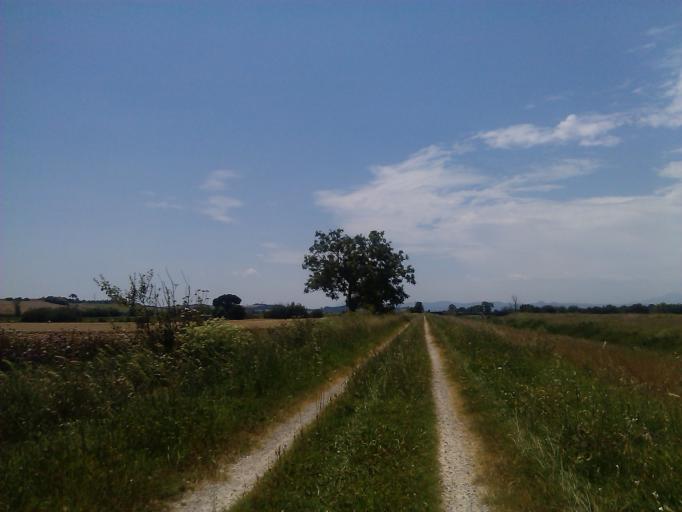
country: IT
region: Tuscany
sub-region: Province of Arezzo
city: Foiano della Chiana
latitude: 43.2853
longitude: 11.8413
